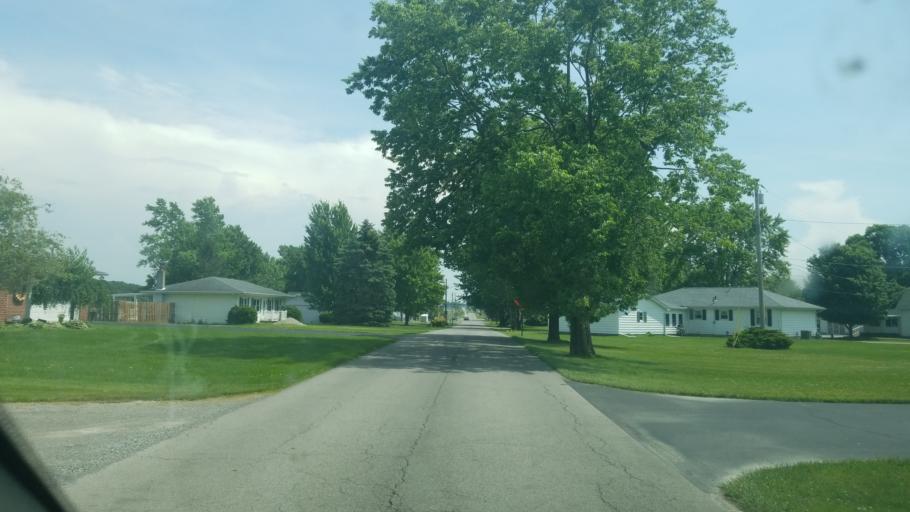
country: US
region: Ohio
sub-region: Logan County
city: Northwood
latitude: 40.5064
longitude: -83.7440
